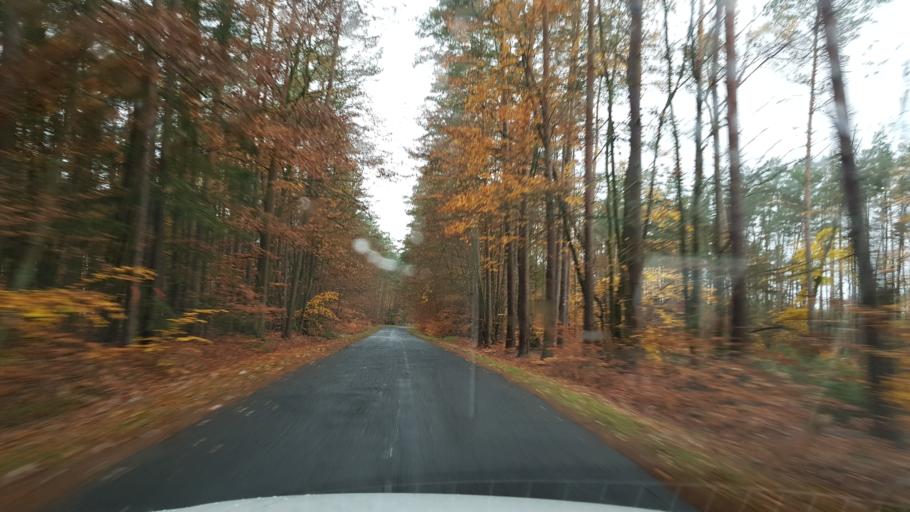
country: PL
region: West Pomeranian Voivodeship
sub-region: Powiat goleniowski
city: Stepnica
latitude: 53.6597
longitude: 14.7033
